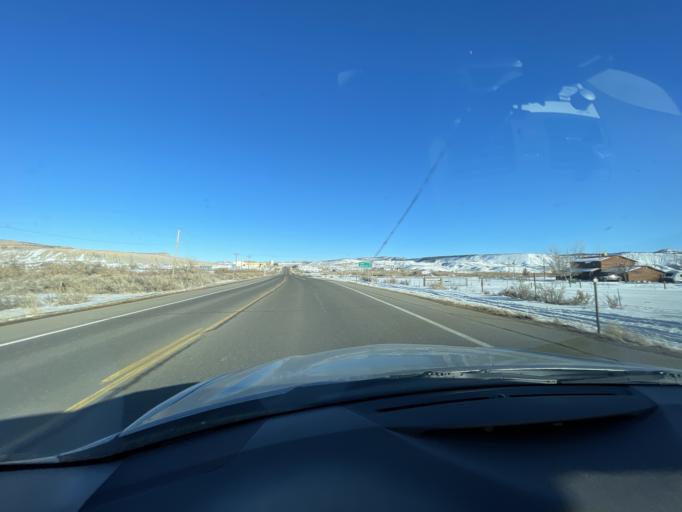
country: US
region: Colorado
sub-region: Rio Blanco County
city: Rangely
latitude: 40.0876
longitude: -108.7786
